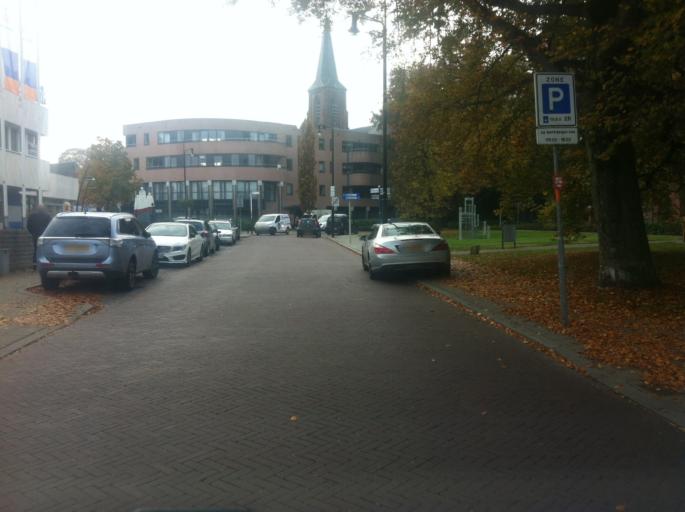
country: NL
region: Gelderland
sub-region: Gemeente Winterswijk
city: Winterswijk
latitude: 51.9735
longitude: 6.7192
